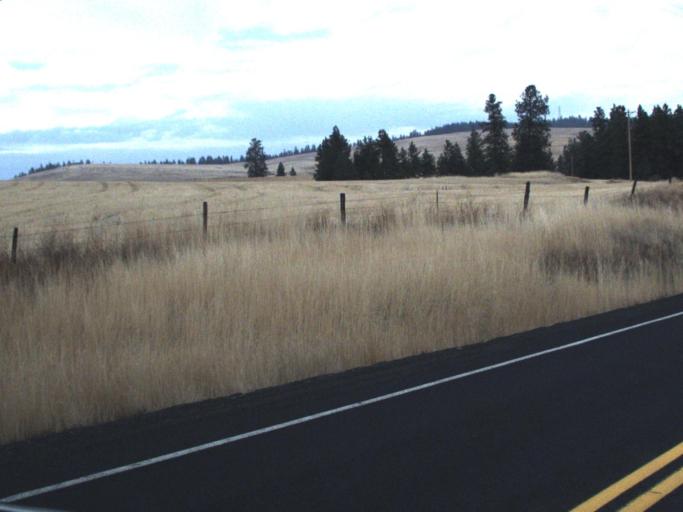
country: US
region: Washington
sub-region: Lincoln County
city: Davenport
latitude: 47.8609
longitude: -118.2359
